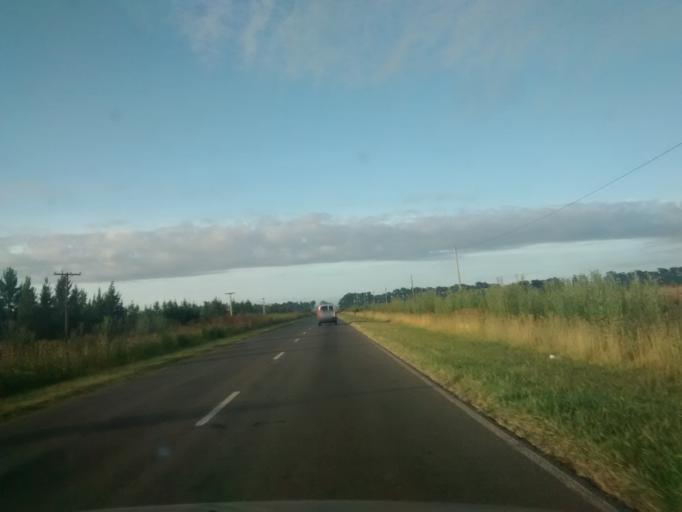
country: AR
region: Buenos Aires
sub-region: Partido de Brandsen
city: Brandsen
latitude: -35.1224
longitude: -58.1893
